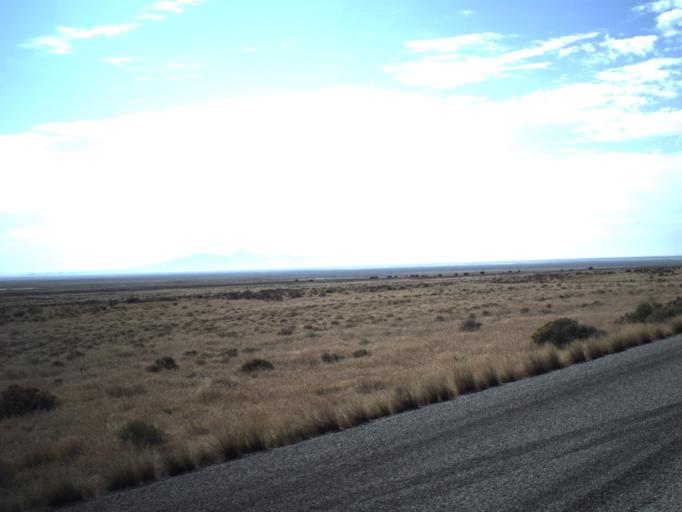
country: US
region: Utah
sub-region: Tooele County
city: Wendover
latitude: 41.5165
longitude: -113.5988
